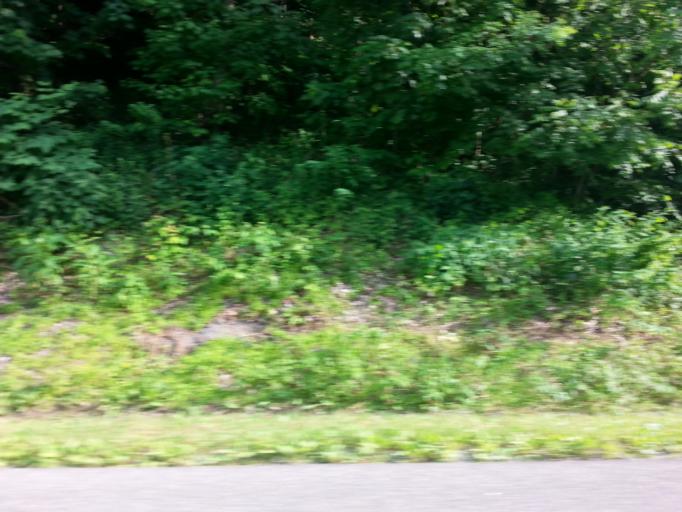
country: US
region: Tennessee
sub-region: Sevier County
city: Gatlinburg
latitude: 35.6732
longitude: -83.5745
